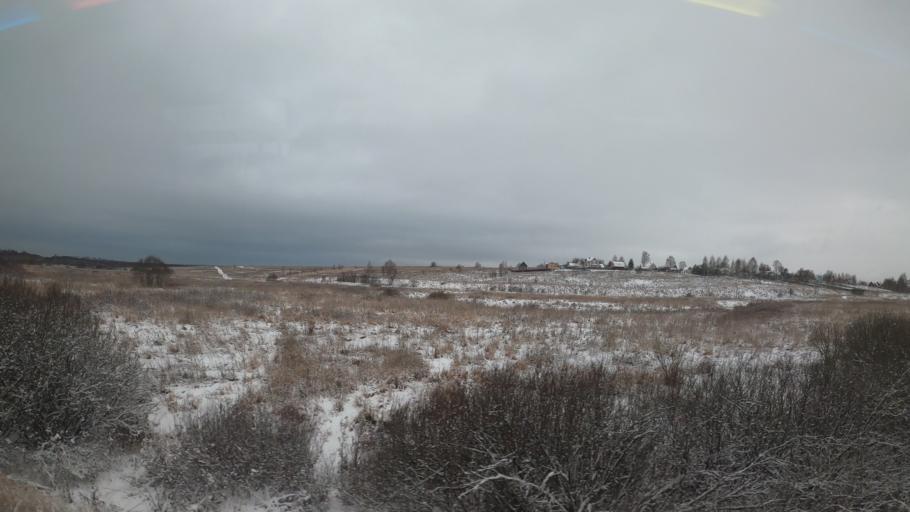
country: RU
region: Jaroslavl
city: Pereslavl'-Zalesskiy
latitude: 56.6998
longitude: 38.9145
